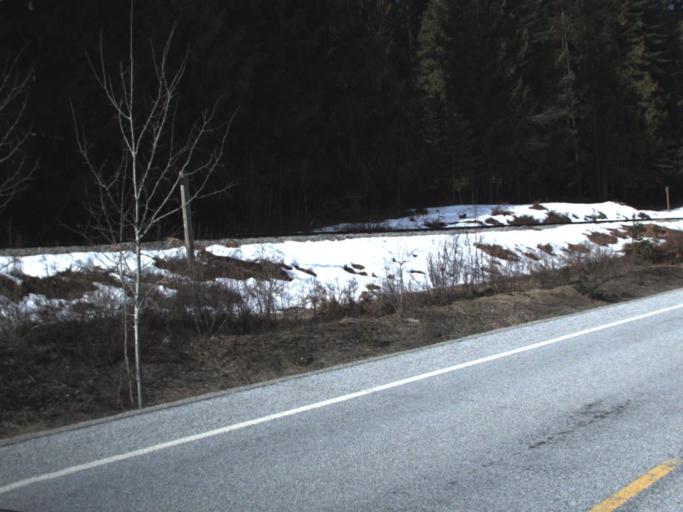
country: US
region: Washington
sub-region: Pend Oreille County
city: Newport
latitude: 48.2323
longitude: -117.2129
